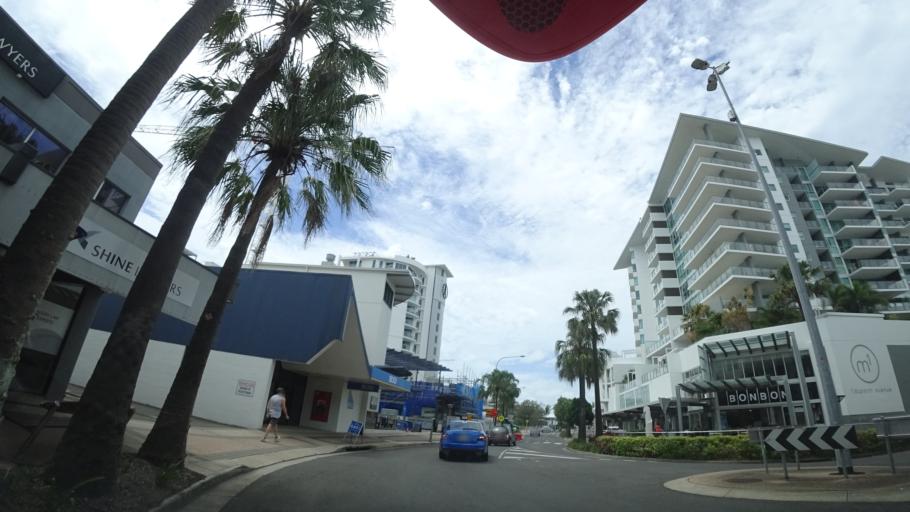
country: AU
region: Queensland
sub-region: Sunshine Coast
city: Mooloolaba
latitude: -26.6526
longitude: 153.0928
